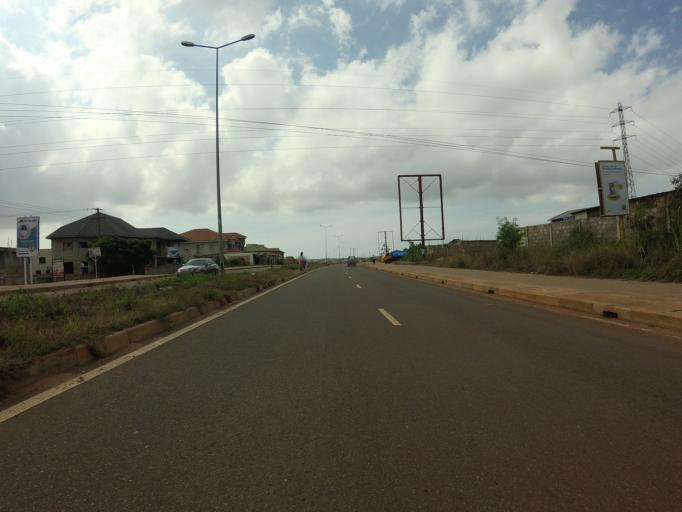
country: GH
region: Greater Accra
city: Teshi Old Town
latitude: 5.6023
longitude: -0.1375
